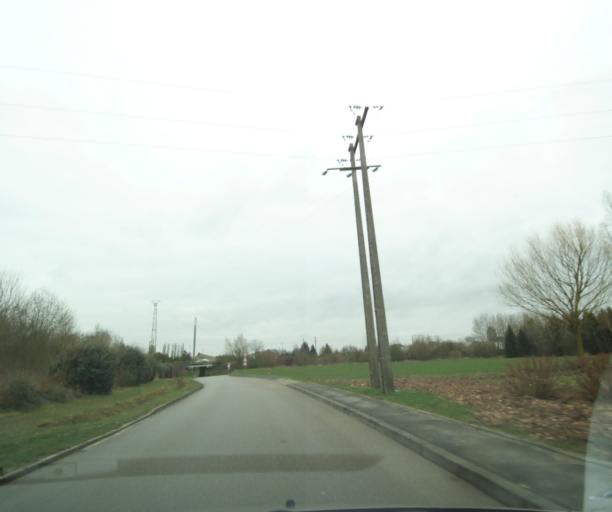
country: FR
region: Picardie
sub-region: Departement de l'Oise
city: Noyon
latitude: 49.5723
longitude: 2.9969
